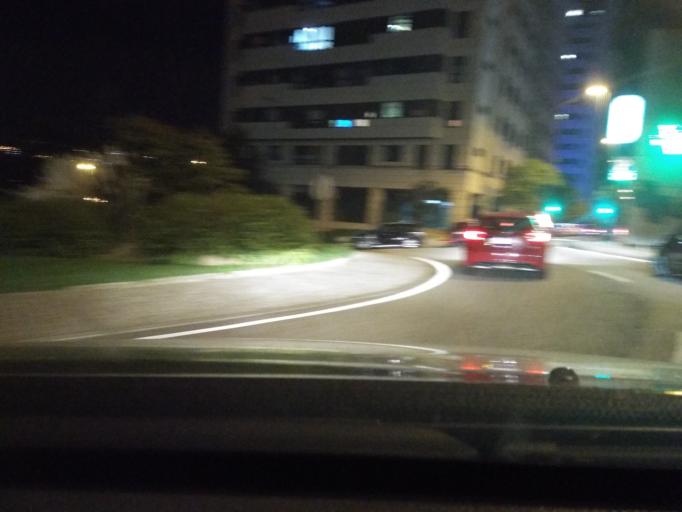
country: ES
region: Galicia
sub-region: Provincia de Pontevedra
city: Vigo
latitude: 42.2209
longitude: -8.7231
